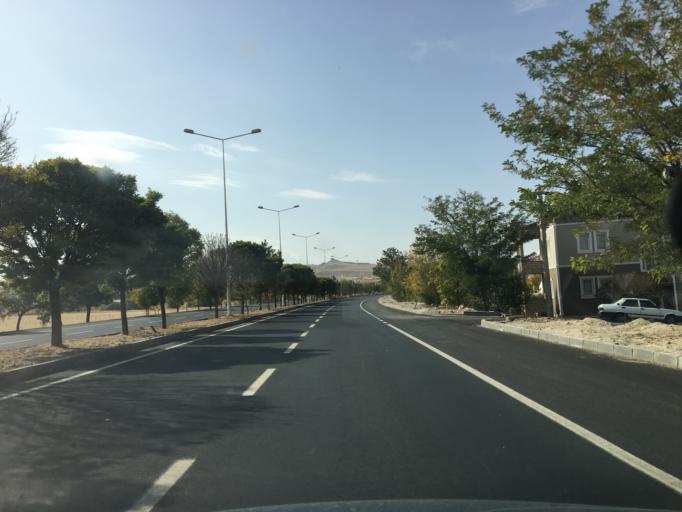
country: TR
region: Nevsehir
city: Avanos
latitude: 38.7040
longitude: 34.8497
